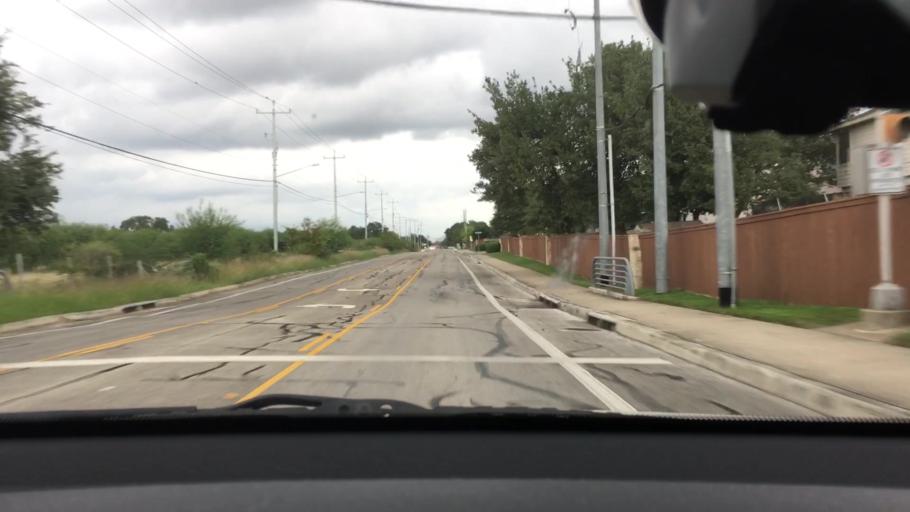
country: US
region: Texas
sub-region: Bexar County
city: Converse
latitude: 29.5317
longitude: -98.3119
